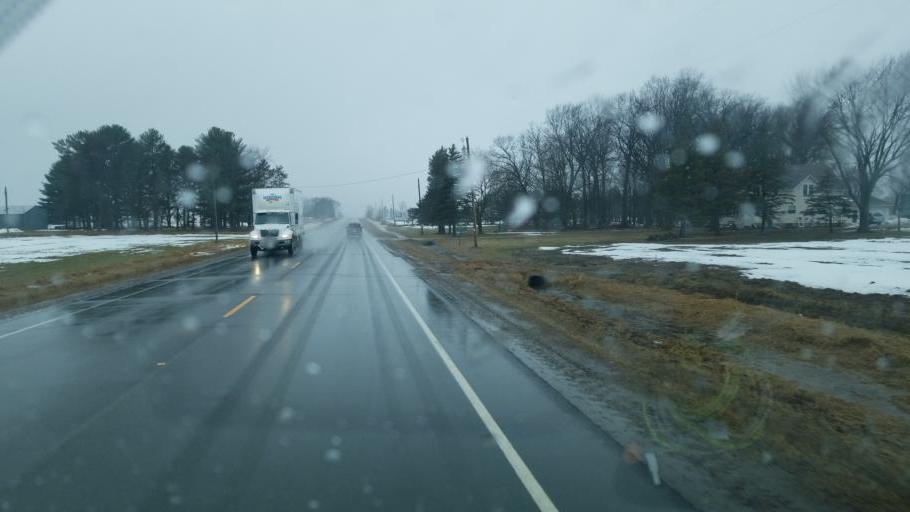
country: US
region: Wisconsin
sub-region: Marathon County
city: Spencer
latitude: 44.6561
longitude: -90.3240
